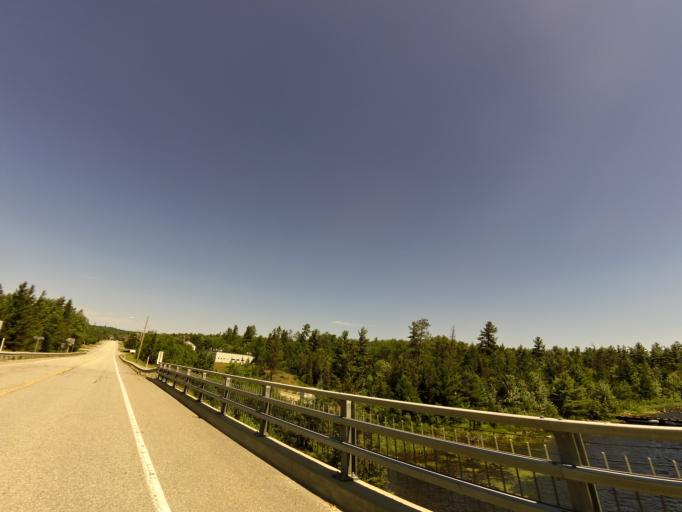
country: CA
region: Quebec
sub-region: Abitibi-Temiscamingue
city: Temiscaming
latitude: 46.7402
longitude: -79.0678
